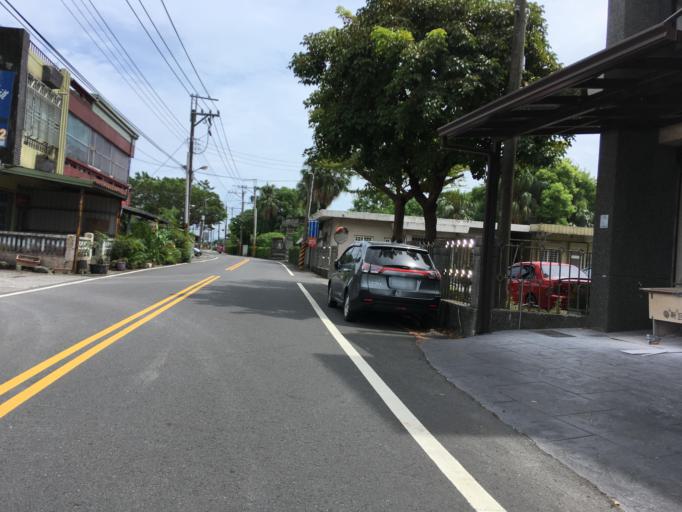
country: TW
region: Taiwan
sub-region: Yilan
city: Yilan
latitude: 24.6960
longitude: 121.8112
